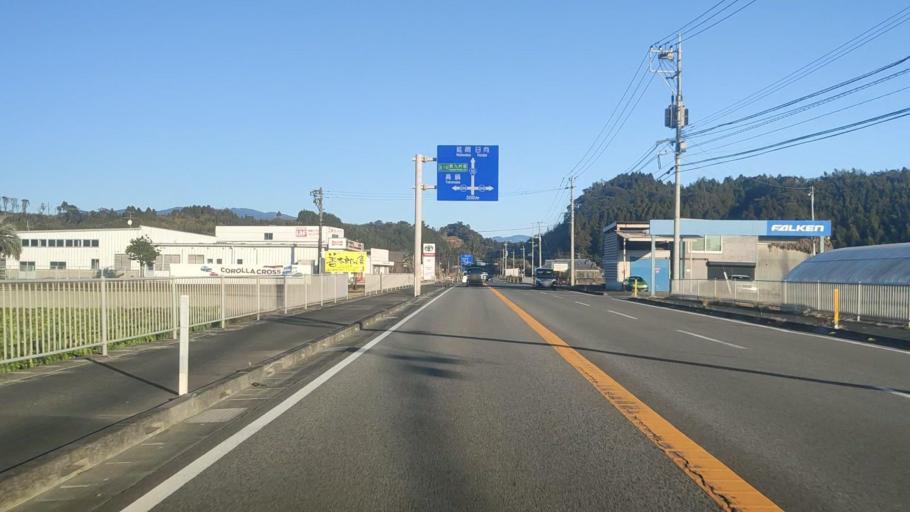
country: JP
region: Miyazaki
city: Takanabe
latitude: 32.1424
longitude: 131.5269
